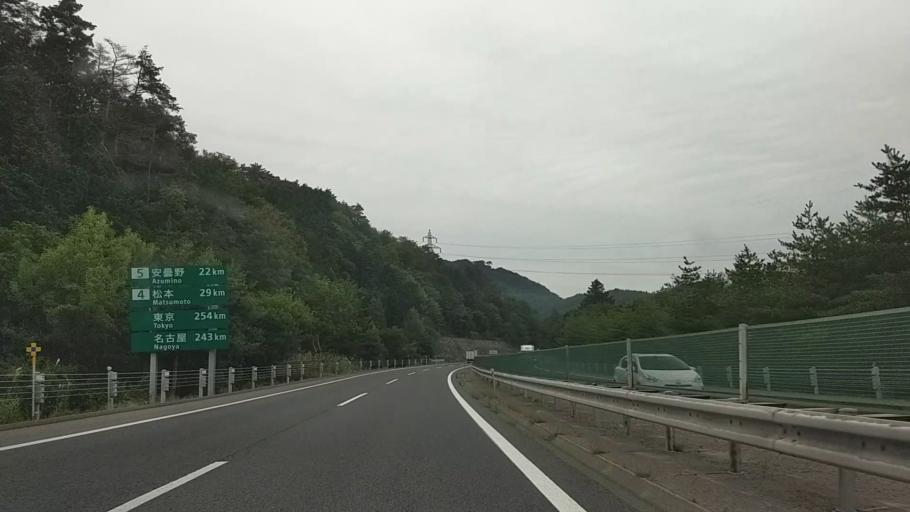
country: JP
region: Nagano
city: Omachi
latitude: 36.4438
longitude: 138.0406
